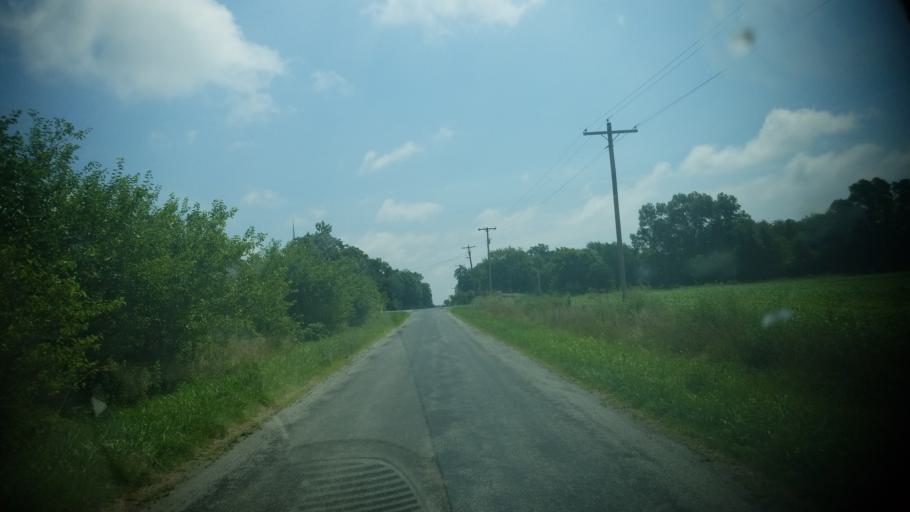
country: US
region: Illinois
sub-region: Wayne County
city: Fairfield
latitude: 38.5223
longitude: -88.3594
